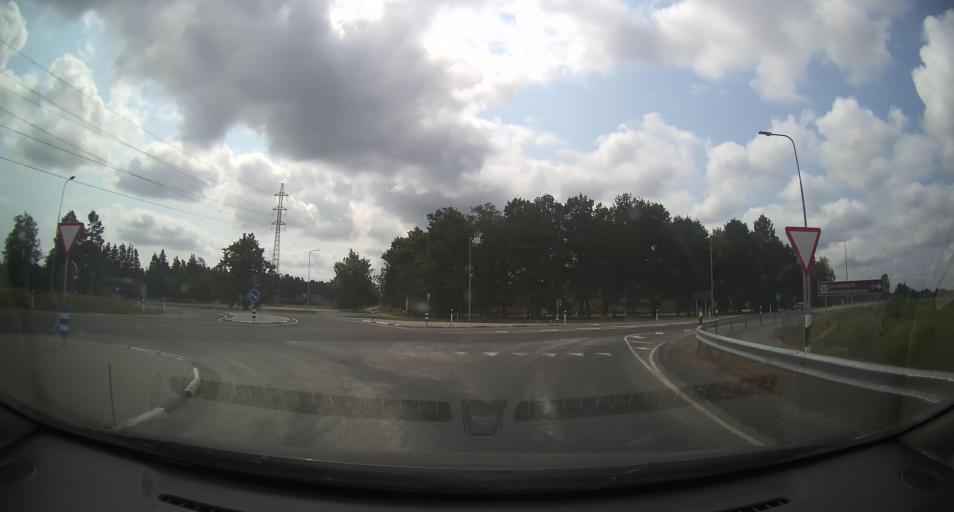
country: EE
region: Paernumaa
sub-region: Audru vald
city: Audru
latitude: 58.4243
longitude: 24.3151
